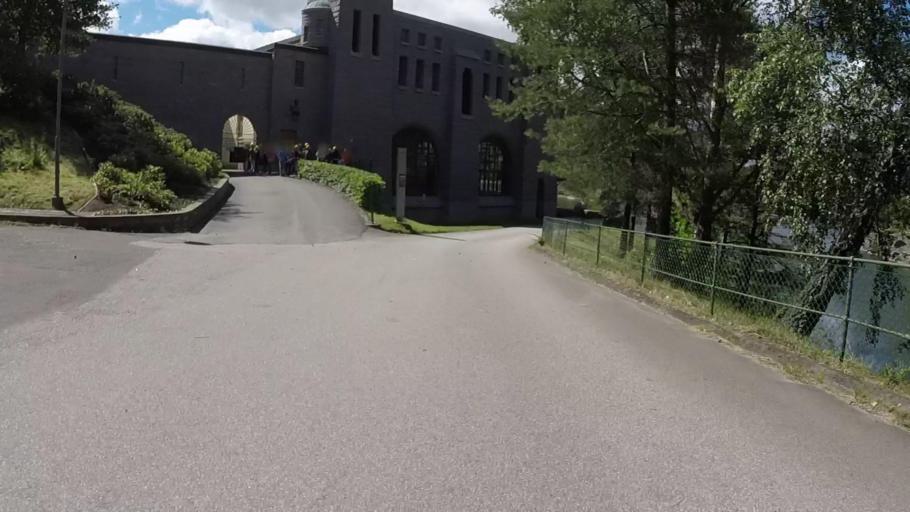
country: SE
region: Vaestra Goetaland
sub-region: Trollhattan
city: Trollhattan
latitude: 58.2760
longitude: 12.2730
